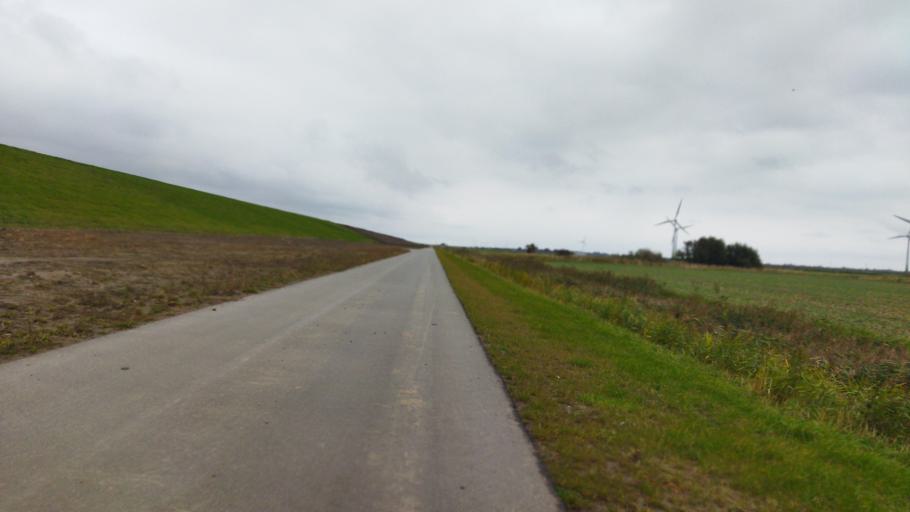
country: NL
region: Groningen
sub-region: Gemeente Delfzijl
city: Delfzijl
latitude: 53.4374
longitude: 7.0185
